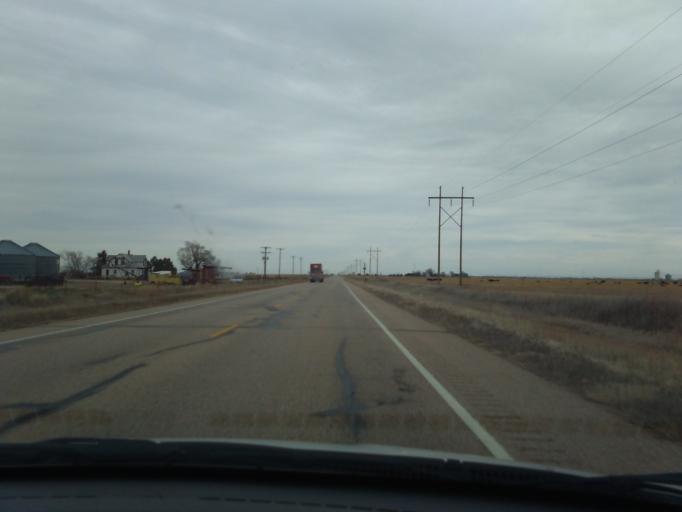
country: US
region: Colorado
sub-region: Yuma County
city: Yuma
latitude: 40.1482
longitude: -102.8628
